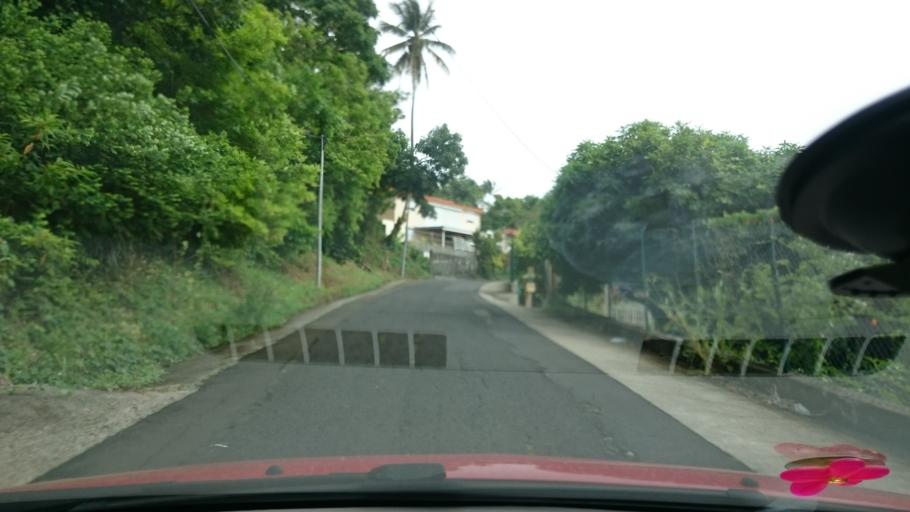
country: MQ
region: Martinique
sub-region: Martinique
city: Riviere-Pilote
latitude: 14.4919
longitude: -60.9100
